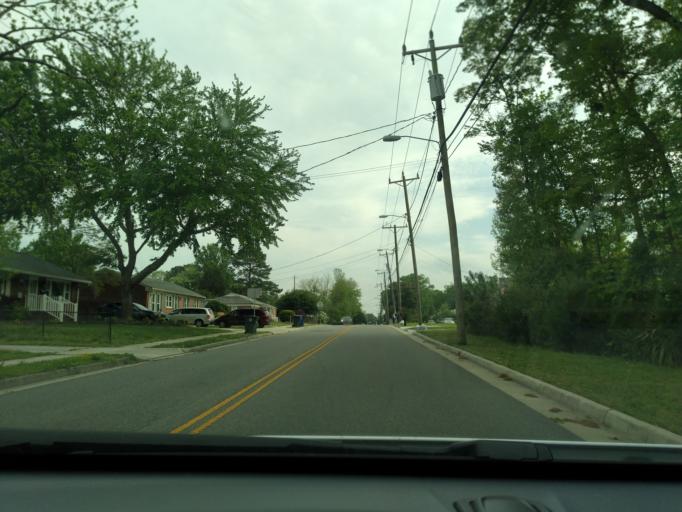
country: US
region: Virginia
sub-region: York County
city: Yorktown
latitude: 37.1561
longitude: -76.5270
